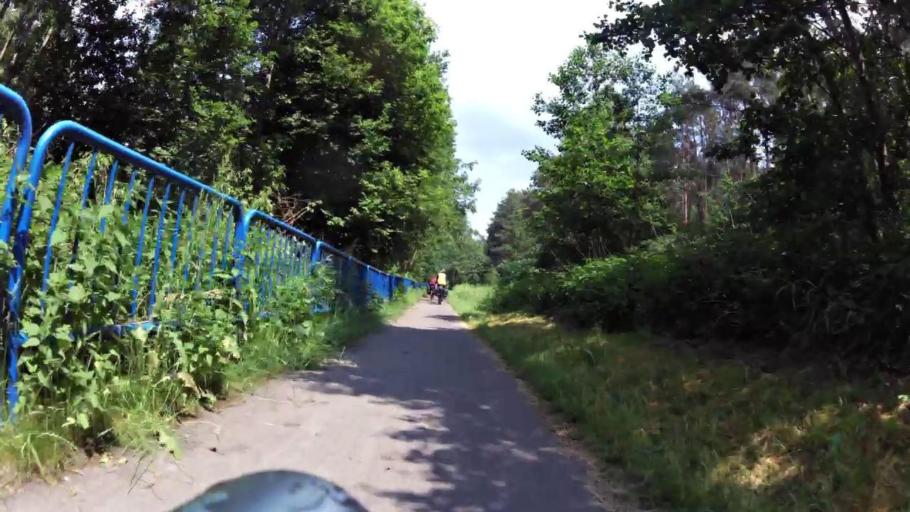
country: PL
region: Kujawsko-Pomorskie
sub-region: Powiat bydgoski
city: Koronowo
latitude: 53.2860
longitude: 17.9444
